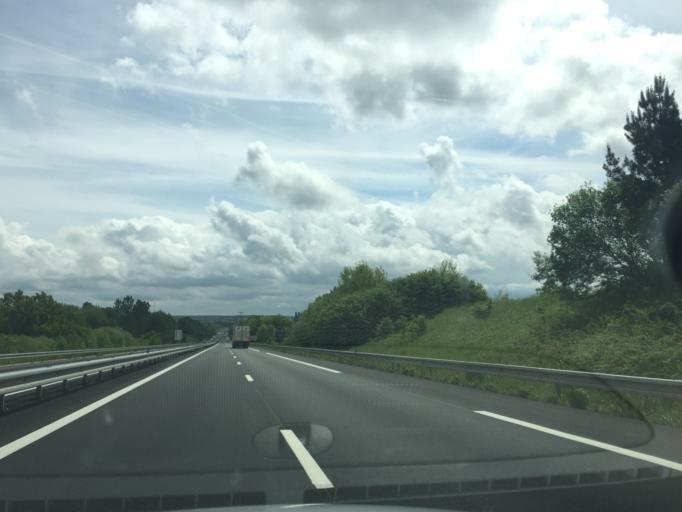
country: FR
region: Pays de la Loire
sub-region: Departement de la Sarthe
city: Ecommoy
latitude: 47.8362
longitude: 0.3057
